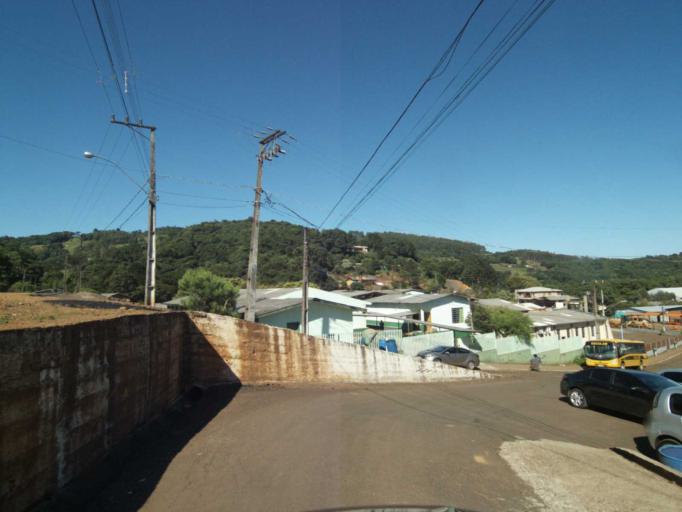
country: BR
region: Parana
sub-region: Francisco Beltrao
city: Francisco Beltrao
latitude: -26.1452
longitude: -53.3123
